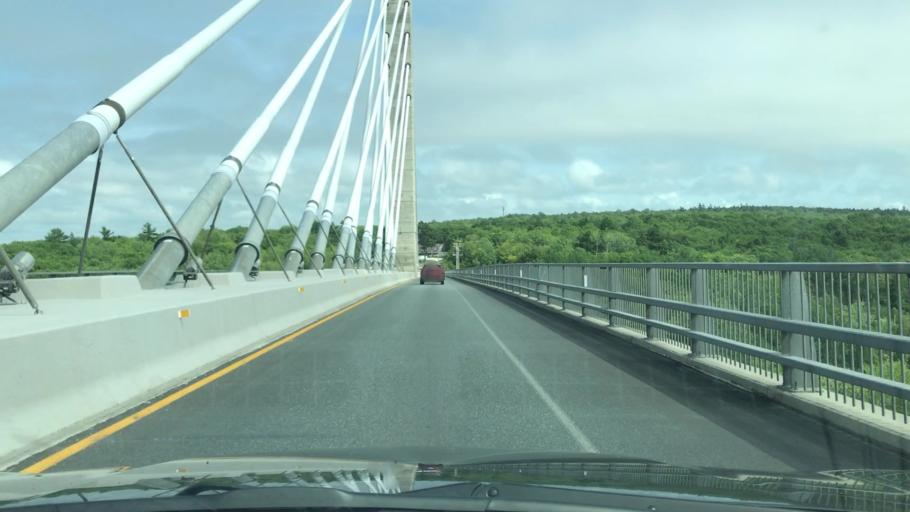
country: US
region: Maine
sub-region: Hancock County
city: Bucksport
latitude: 44.5599
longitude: -68.8014
